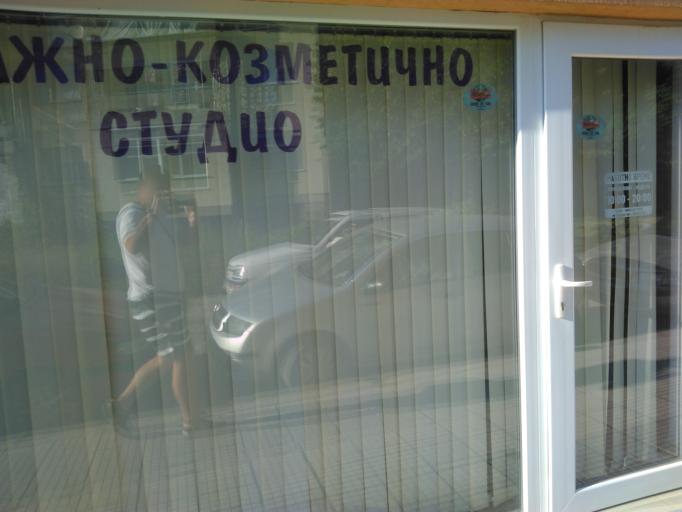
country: BG
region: Plovdiv
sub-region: Obshtina Plovdiv
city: Plovdiv
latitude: 42.1512
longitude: 24.7564
